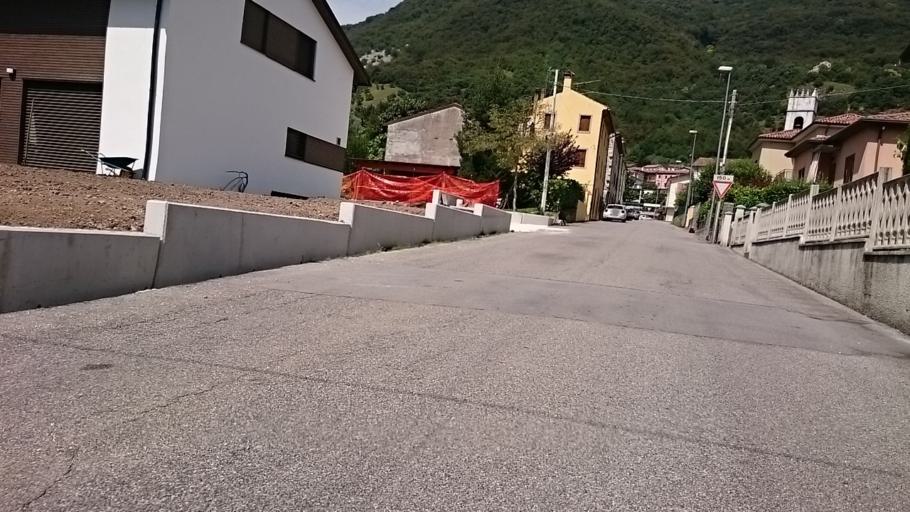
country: IT
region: Veneto
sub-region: Provincia di Treviso
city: Revine
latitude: 46.0053
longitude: 12.2735
